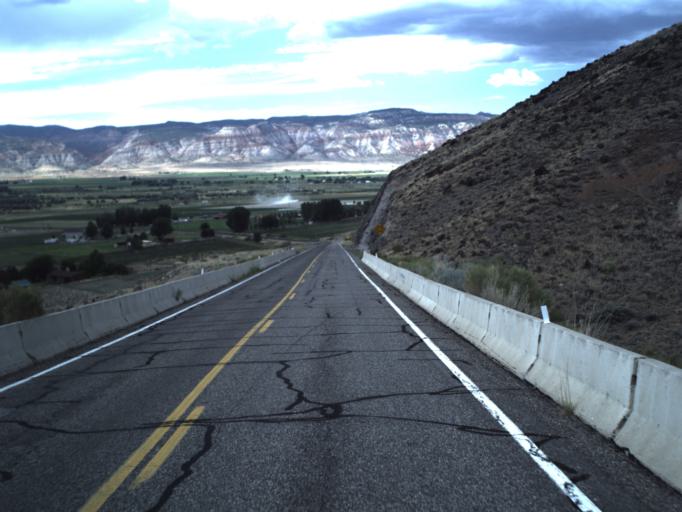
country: US
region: Utah
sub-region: Sevier County
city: Richfield
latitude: 38.7691
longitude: -111.9804
